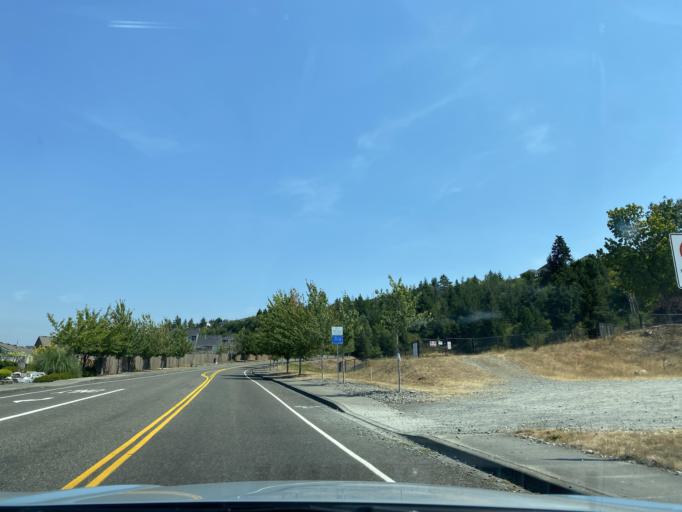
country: US
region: Washington
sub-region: Pierce County
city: Bonney Lake
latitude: 47.1548
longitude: -122.2006
